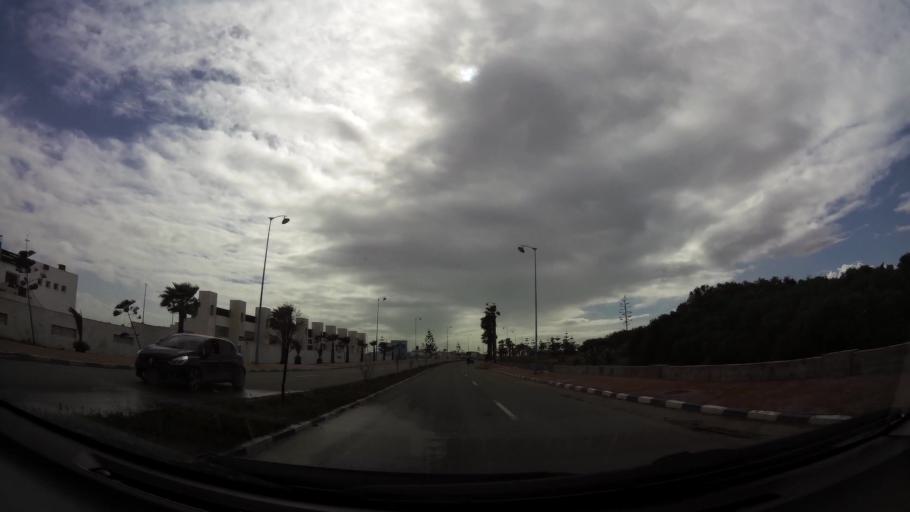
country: MA
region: Doukkala-Abda
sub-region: El-Jadida
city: El Jadida
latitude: 33.2444
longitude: -8.4642
